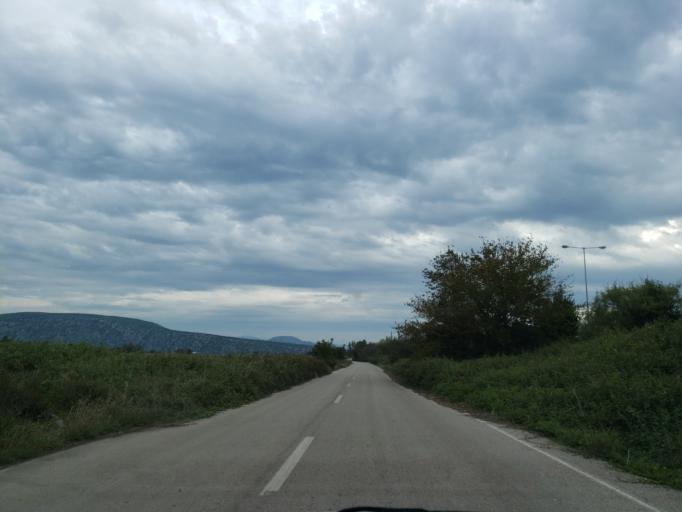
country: GR
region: Central Greece
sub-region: Nomos Voiotias
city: Akraifnia
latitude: 38.4829
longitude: 23.1643
